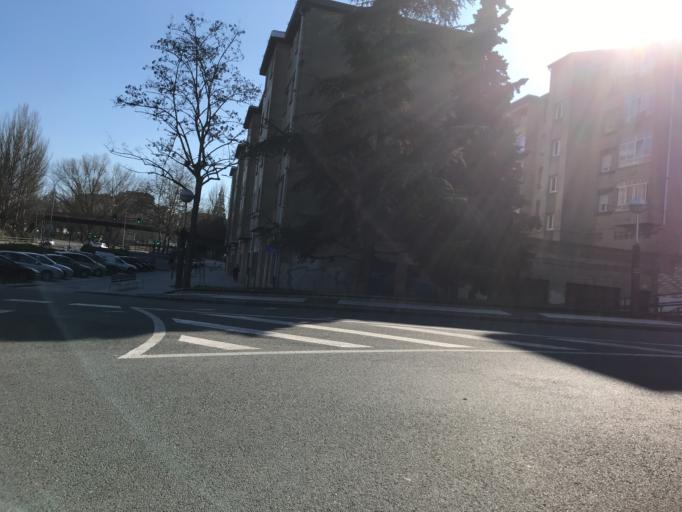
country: ES
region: Basque Country
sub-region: Provincia de Alava
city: Gasteiz / Vitoria
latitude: 42.8508
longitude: -2.6580
